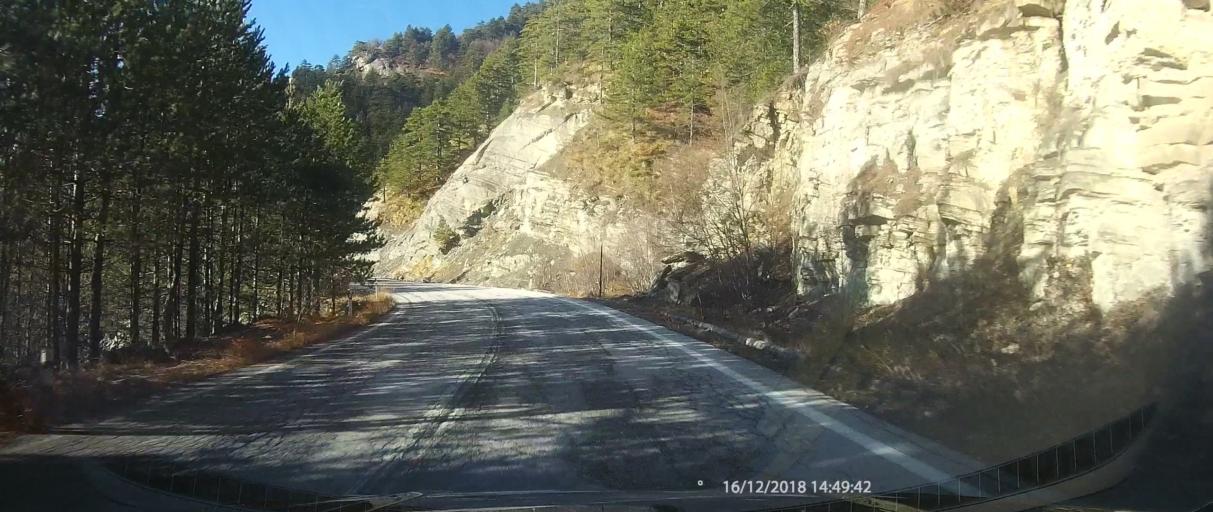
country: GR
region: West Macedonia
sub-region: Nomos Kastorias
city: Nestorio
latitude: 40.2089
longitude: 21.0860
